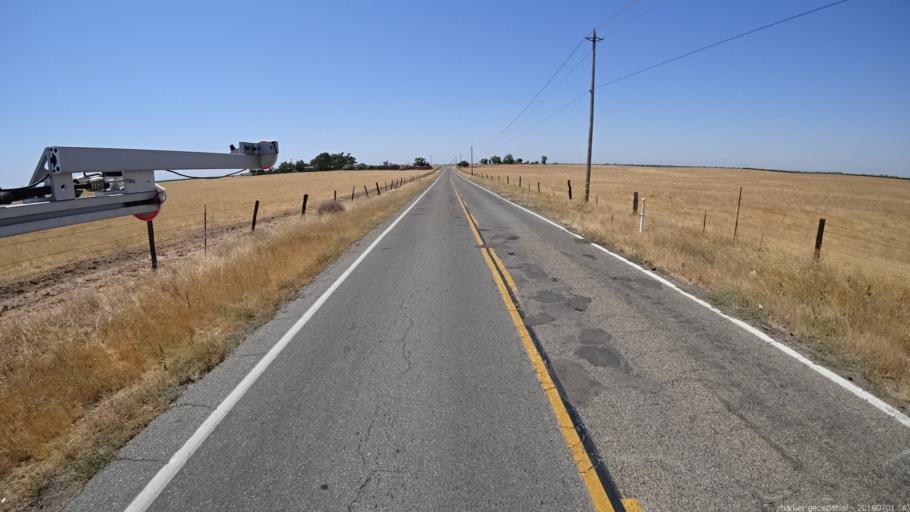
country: US
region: California
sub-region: Madera County
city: Madera Acres
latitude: 37.0266
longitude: -120.0290
